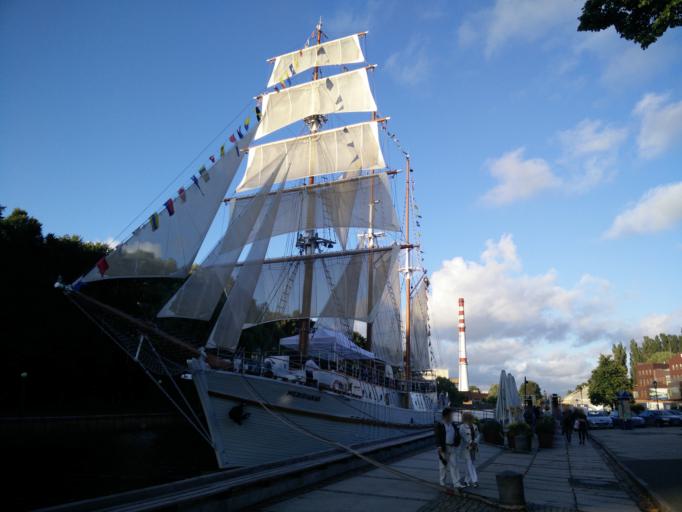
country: LT
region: Klaipedos apskritis
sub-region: Klaipeda
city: Klaipeda
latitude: 55.7102
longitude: 21.1343
